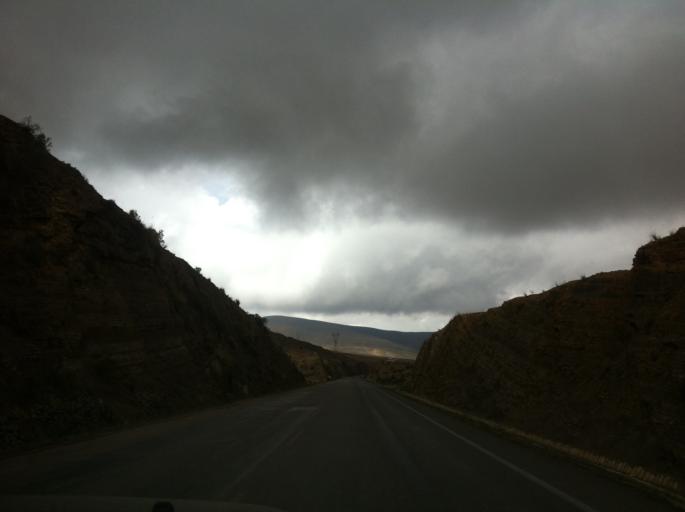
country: BO
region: Cochabamba
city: Irpa Irpa
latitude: -17.6930
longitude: -66.5154
